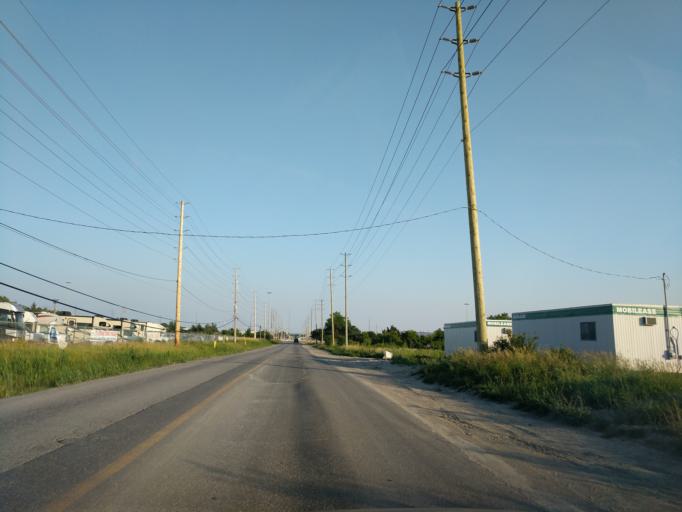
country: CA
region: Ontario
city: Oshawa
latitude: 43.8773
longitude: -78.8868
